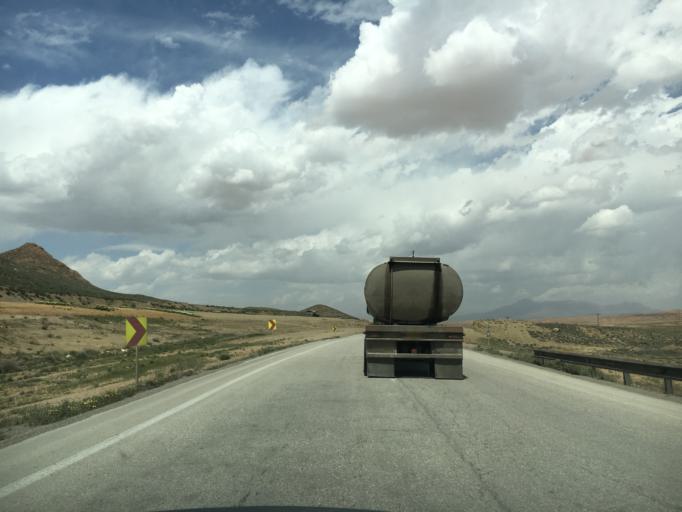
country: IR
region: Markazi
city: Delijan
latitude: 33.6130
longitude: 50.9963
